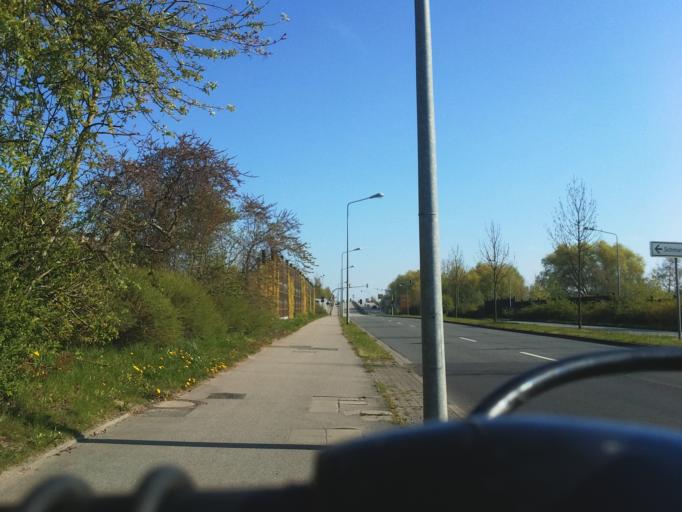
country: DE
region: Mecklenburg-Vorpommern
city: Warnemuende
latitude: 54.1329
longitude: 12.0769
